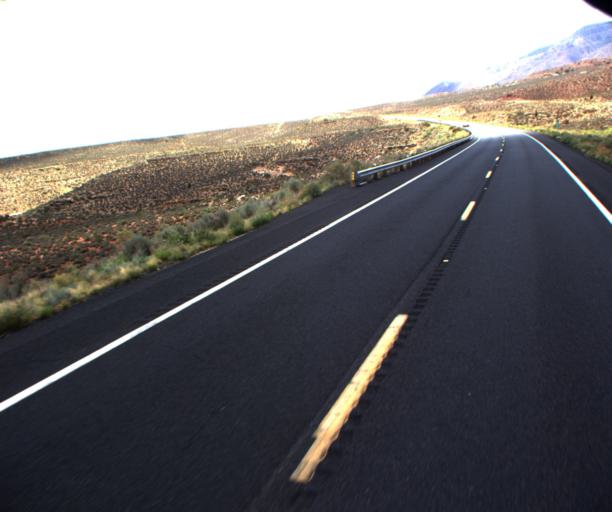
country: US
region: Arizona
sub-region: Coconino County
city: Tuba City
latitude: 35.9253
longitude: -111.6121
